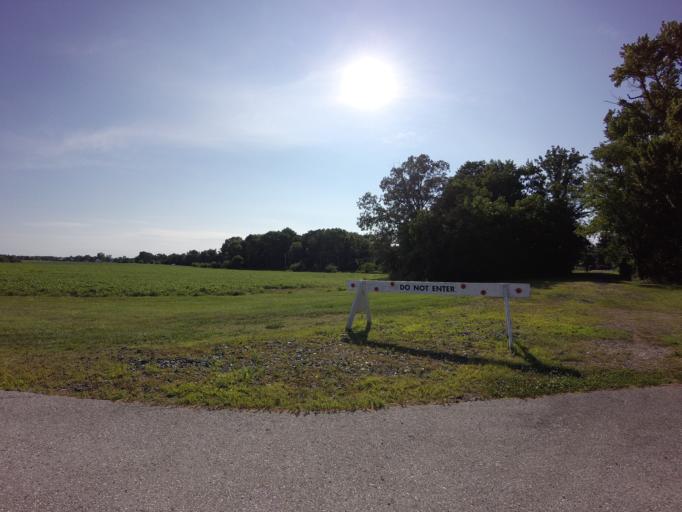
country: US
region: Maryland
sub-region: Baltimore County
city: Edgemere
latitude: 39.2201
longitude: -76.4313
